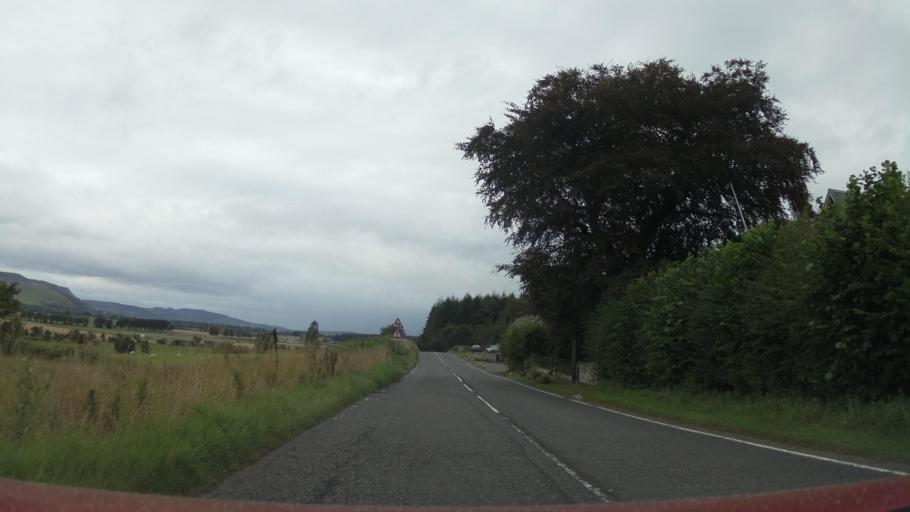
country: GB
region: Scotland
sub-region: Fife
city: Ballingry
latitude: 56.1993
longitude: -3.2907
